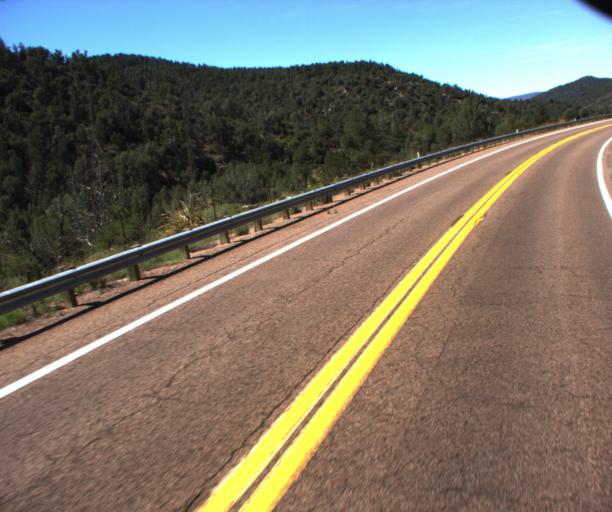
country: US
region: Arizona
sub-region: Navajo County
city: Cibecue
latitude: 33.8425
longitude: -110.4264
